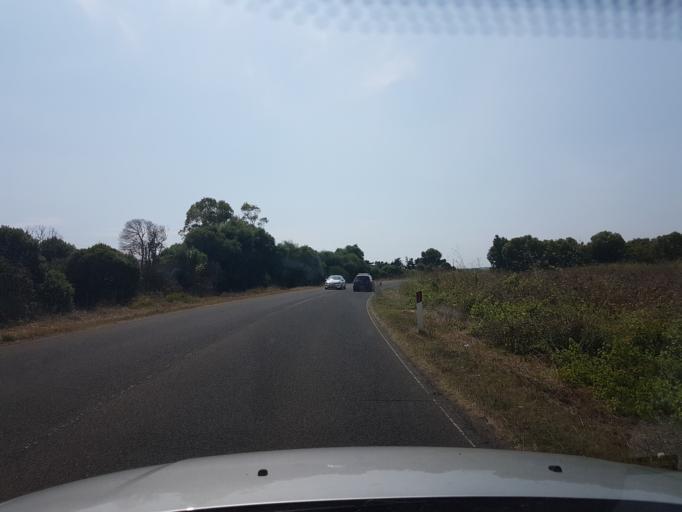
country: IT
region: Sardinia
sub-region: Provincia di Oristano
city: Cabras
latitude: 39.9162
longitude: 8.5028
